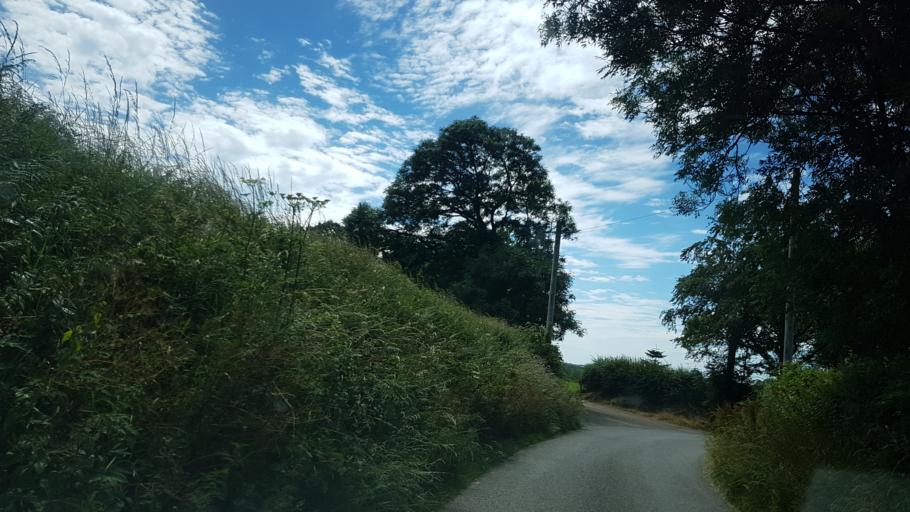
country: GB
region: Wales
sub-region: Pembrokeshire
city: Haverfordwest
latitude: 51.8200
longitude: -4.9346
